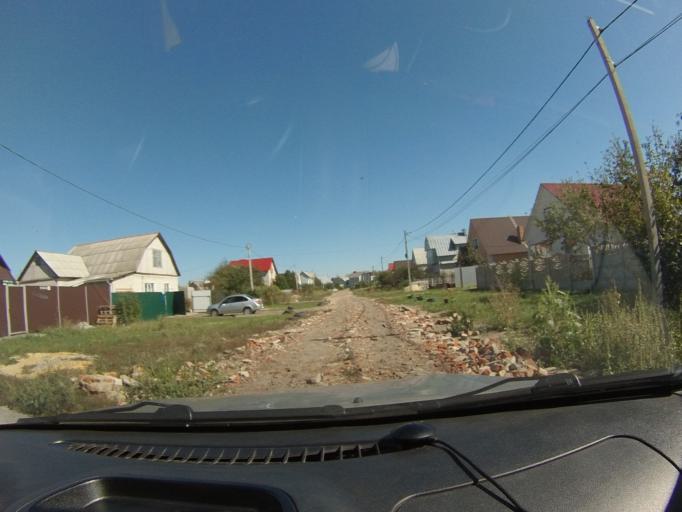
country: RU
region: Tambov
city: Tambov
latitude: 52.7604
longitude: 41.3677
